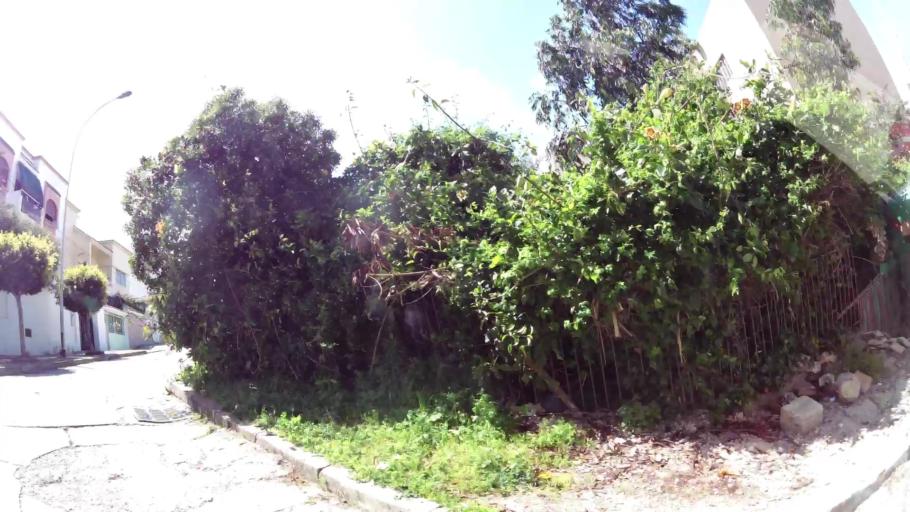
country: MA
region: Tanger-Tetouan
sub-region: Tanger-Assilah
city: Tangier
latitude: 35.7686
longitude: -5.8306
